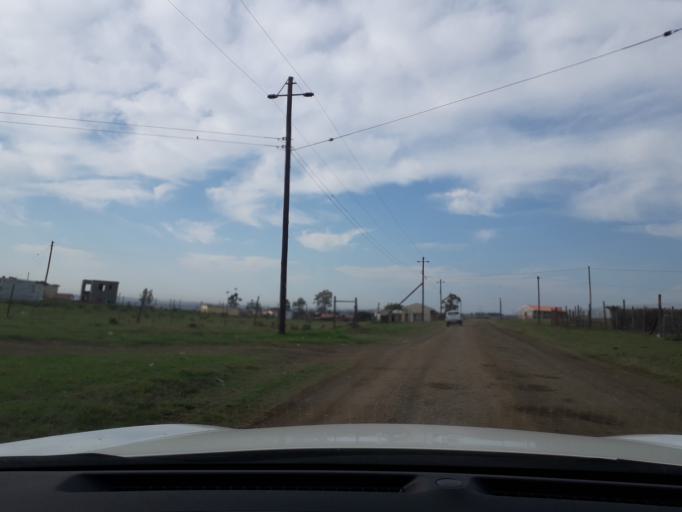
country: ZA
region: Eastern Cape
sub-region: Buffalo City Metropolitan Municipality
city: Bhisho
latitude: -32.9332
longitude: 27.3778
